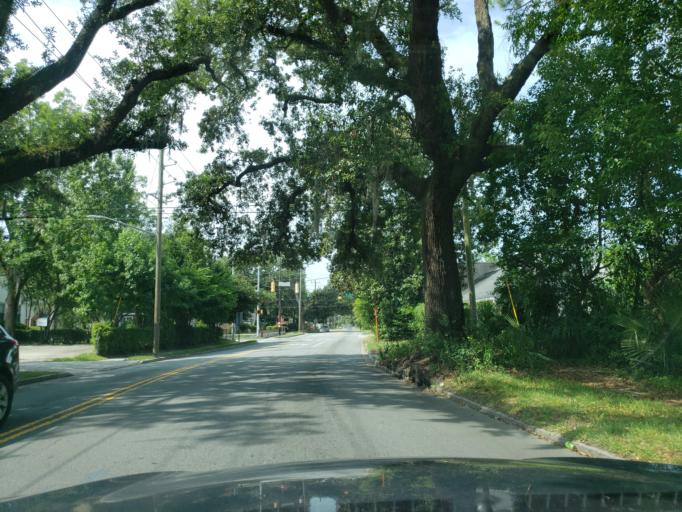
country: US
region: Georgia
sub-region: Chatham County
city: Thunderbolt
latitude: 32.0420
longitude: -81.0875
